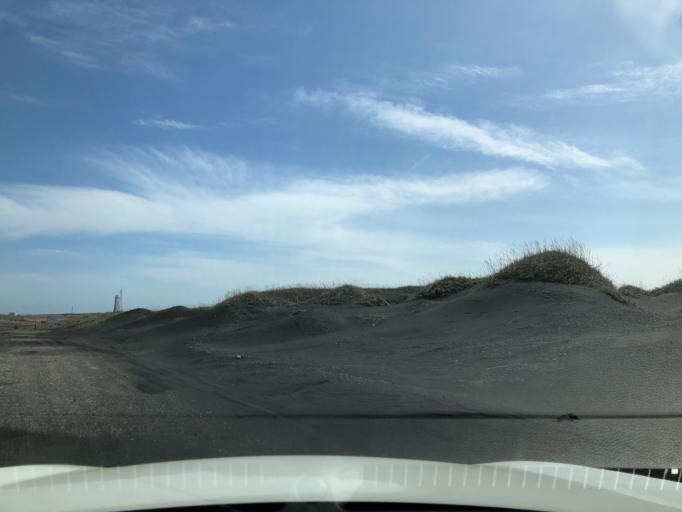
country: IS
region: East
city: Hoefn
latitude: 64.2448
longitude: -14.9729
